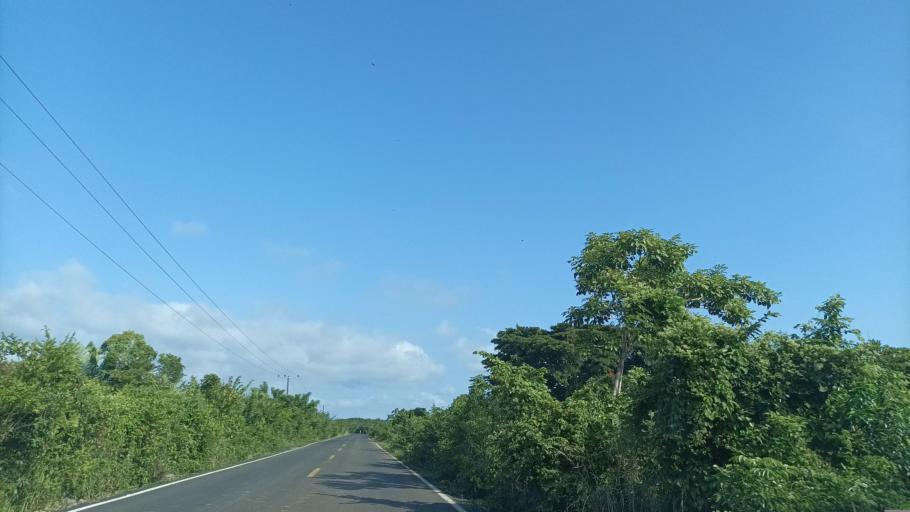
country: MX
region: Veracruz
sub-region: Chinameca
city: Chacalapa
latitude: 18.1437
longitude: -94.6533
